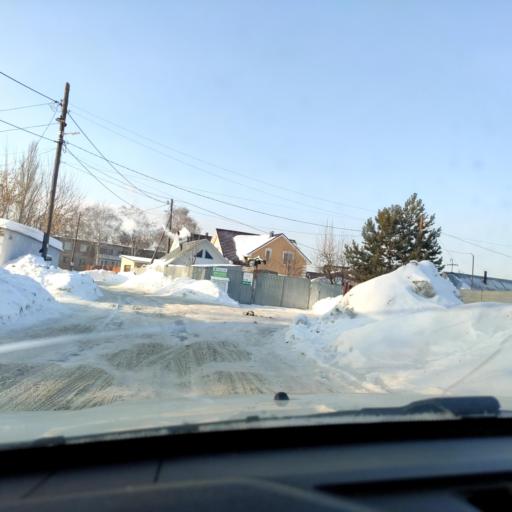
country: RU
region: Samara
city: Petra-Dubrava
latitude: 53.3187
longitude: 50.2902
